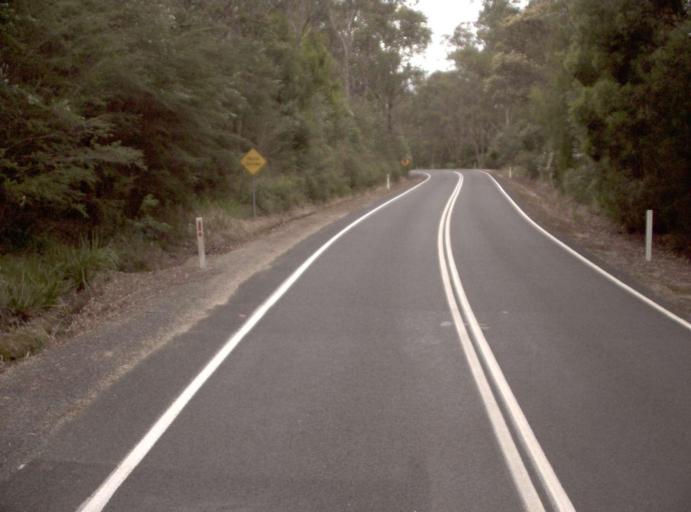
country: AU
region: New South Wales
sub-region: Bombala
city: Bombala
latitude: -37.3378
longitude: 149.2063
